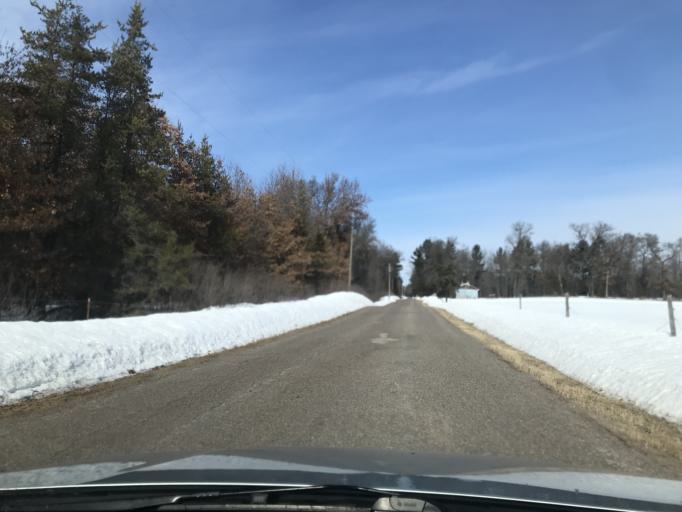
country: US
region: Wisconsin
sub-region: Marinette County
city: Peshtigo
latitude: 45.2207
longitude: -87.9629
